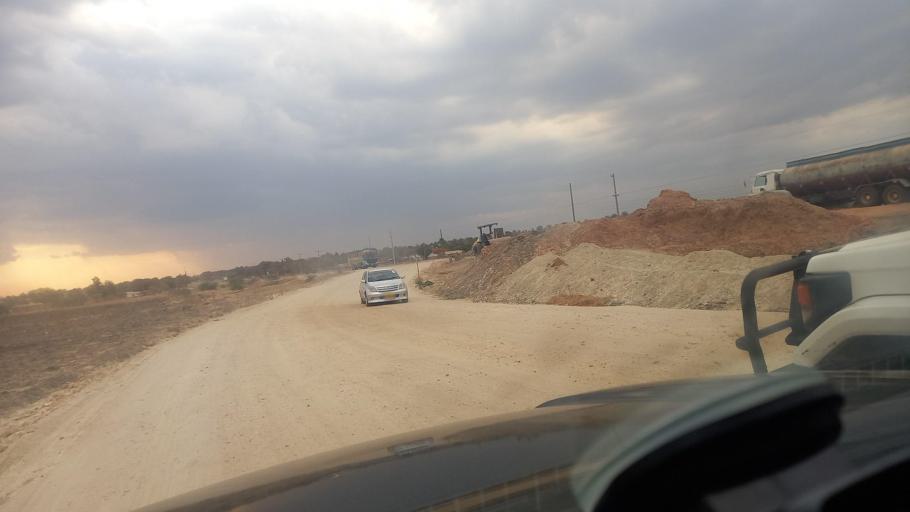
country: TZ
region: Dodoma
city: Kongwa
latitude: -6.0841
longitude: 36.5915
